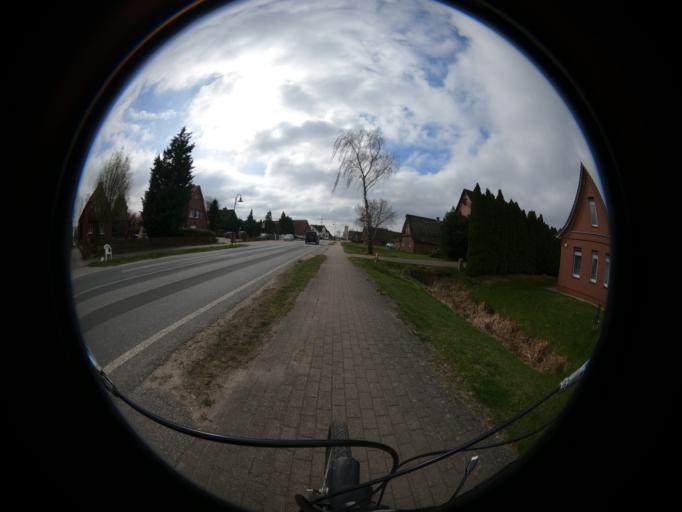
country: DE
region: Lower Saxony
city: Neu Wulmstorf
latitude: 53.4935
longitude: 9.7795
